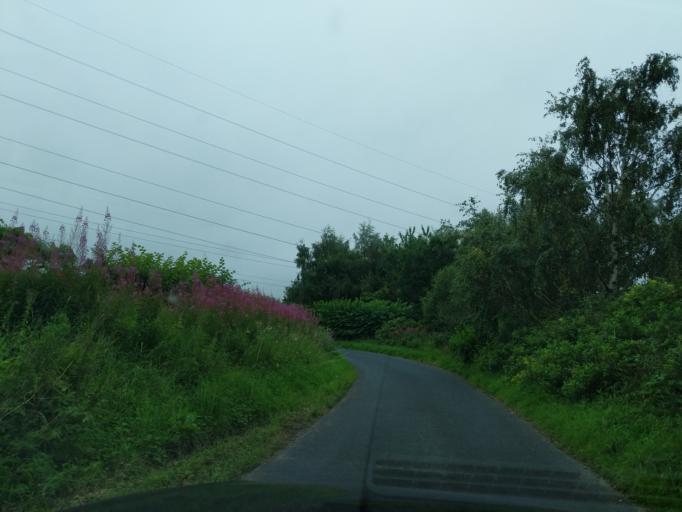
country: GB
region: Scotland
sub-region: East Lothian
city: Ormiston
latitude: 55.8945
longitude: -2.9503
